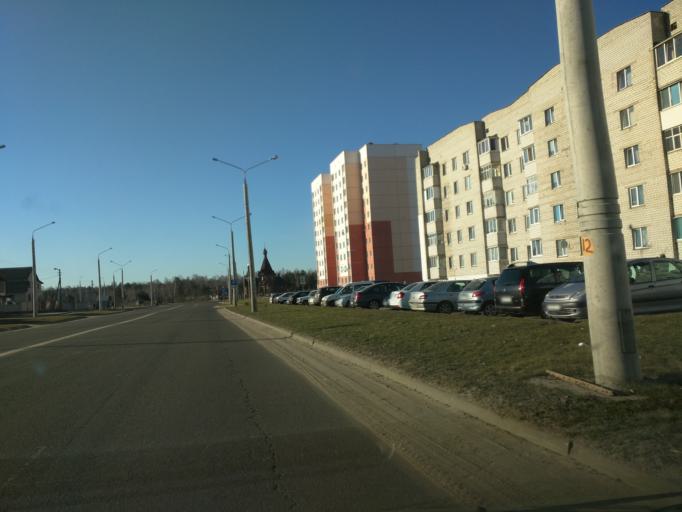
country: BY
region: Mogilev
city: Babruysk
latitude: 53.1658
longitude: 29.1649
